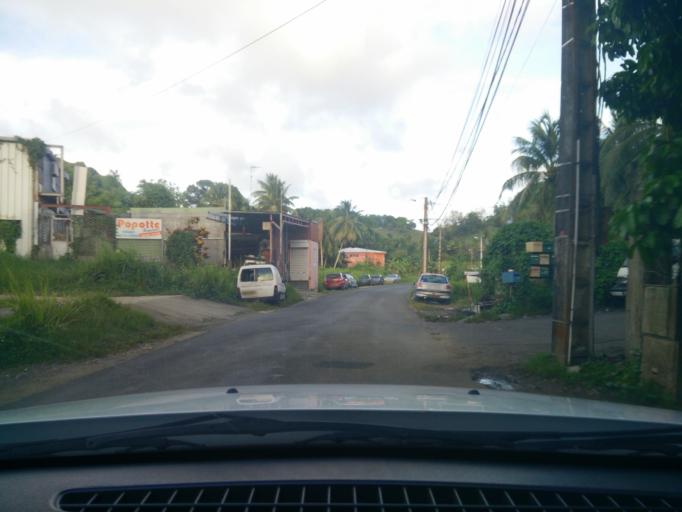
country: GP
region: Guadeloupe
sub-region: Guadeloupe
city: Les Abymes
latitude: 16.2546
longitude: -61.5014
